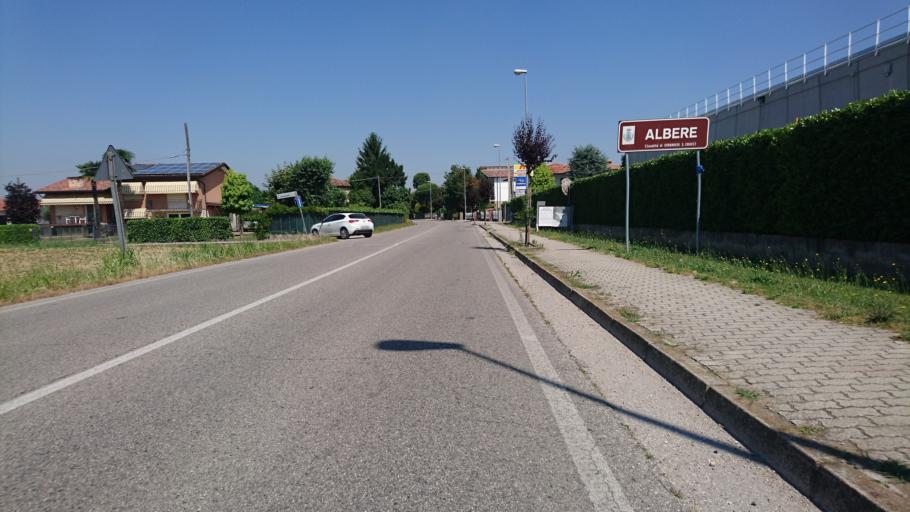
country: IT
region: Veneto
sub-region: Provincia di Padova
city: Montemerlo
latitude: 45.3878
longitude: 11.7022
